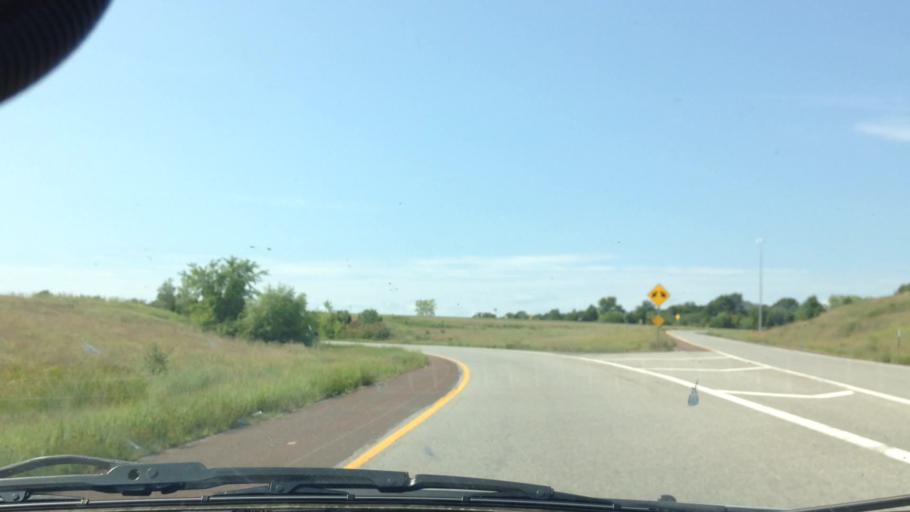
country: US
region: Kansas
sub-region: Wyandotte County
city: Edwardsville
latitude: 39.0132
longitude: -94.7874
